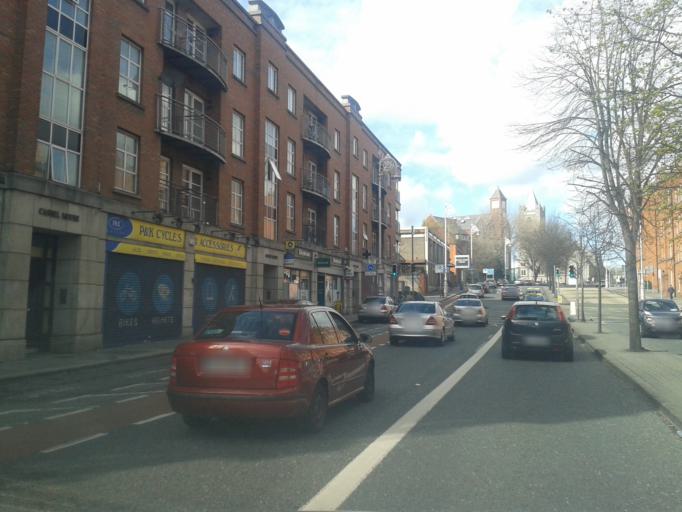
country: IE
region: Leinster
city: Rathmines
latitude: 53.3410
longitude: -6.2723
